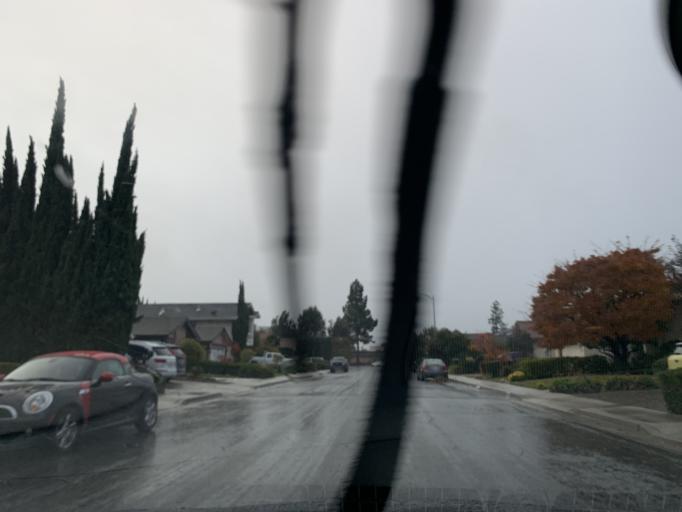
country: US
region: California
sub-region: Santa Clara County
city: Cambrian Park
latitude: 37.2553
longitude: -121.9455
